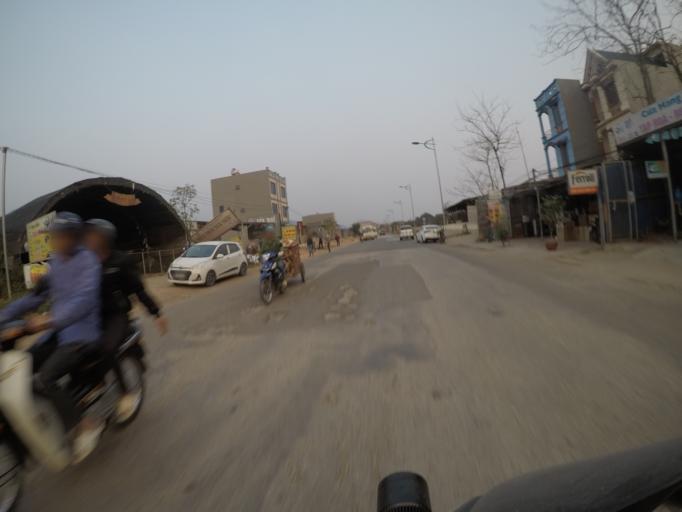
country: VN
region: Vinh Phuc
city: Trai Ngau
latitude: 21.4288
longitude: 105.5886
